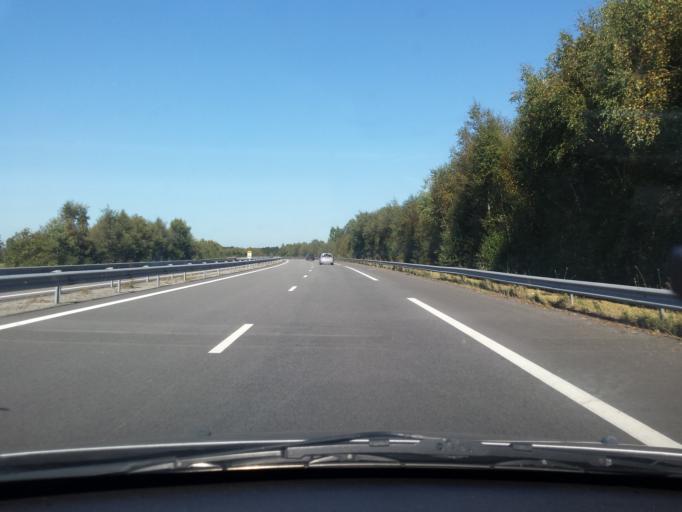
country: FR
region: Brittany
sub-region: Departement du Morbihan
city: Naizin
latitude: 47.9832
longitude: -2.8701
